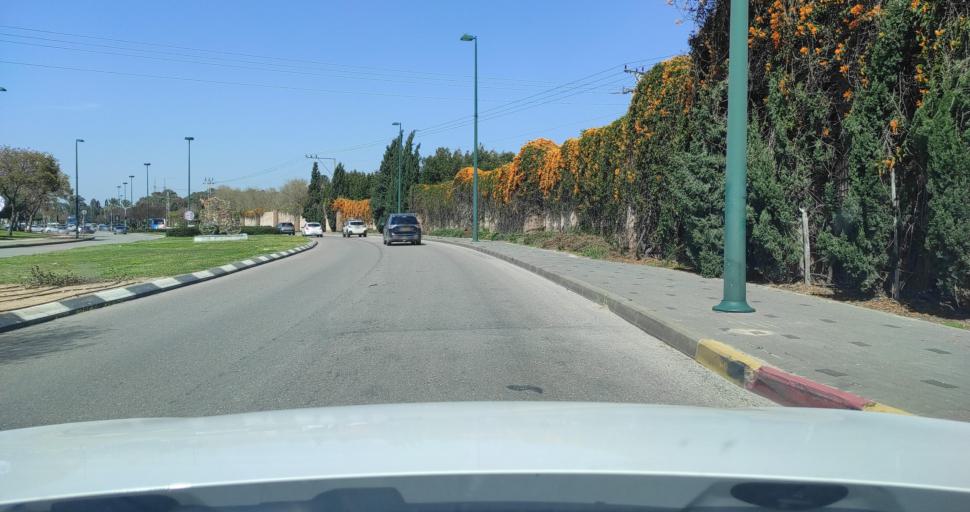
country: IL
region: Central District
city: Bet Yizhaq
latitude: 32.3178
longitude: 34.8823
